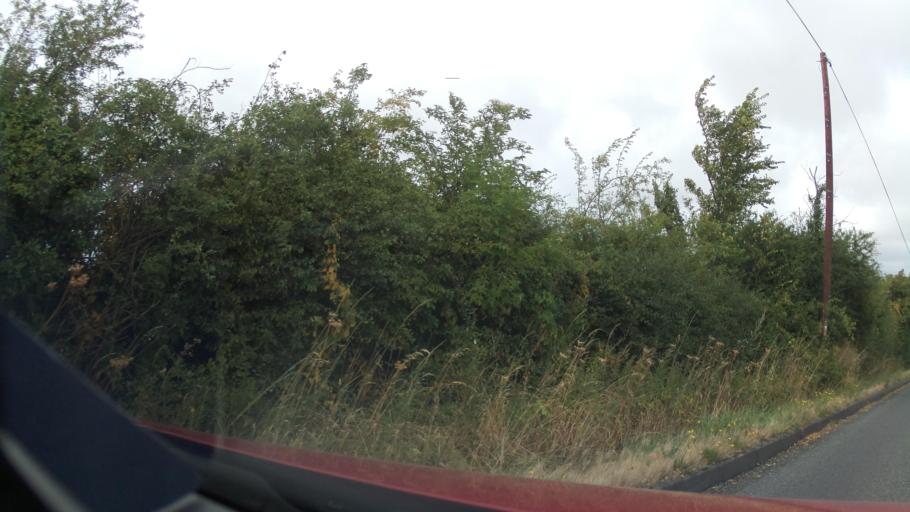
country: GB
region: England
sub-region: Derbyshire
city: Long Eaton
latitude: 52.9223
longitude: -1.3082
